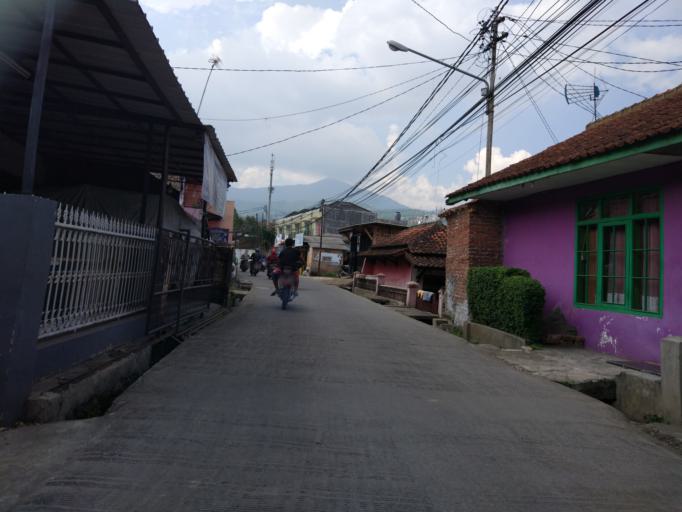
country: ID
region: West Java
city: Cileunyi
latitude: -6.9031
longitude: 107.6910
